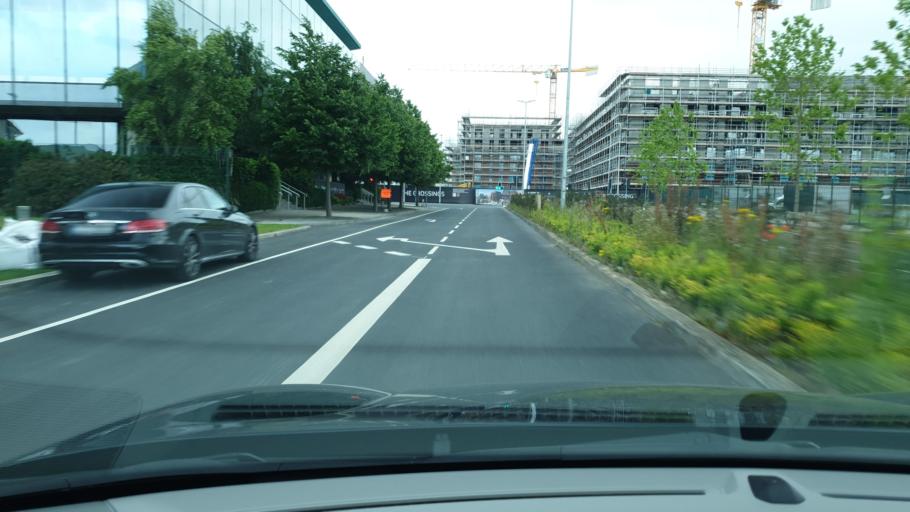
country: IE
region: Leinster
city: Lucan
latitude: 53.3390
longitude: -6.4694
